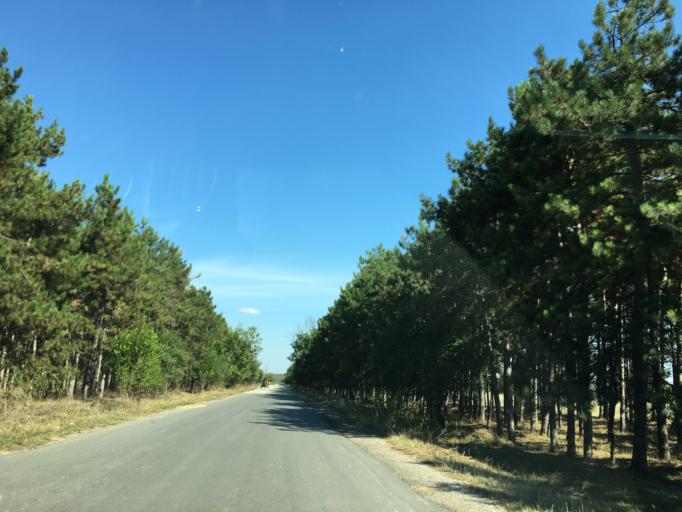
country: BG
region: Pleven
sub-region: Obshtina Knezha
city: Knezha
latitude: 43.5149
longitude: 24.0964
